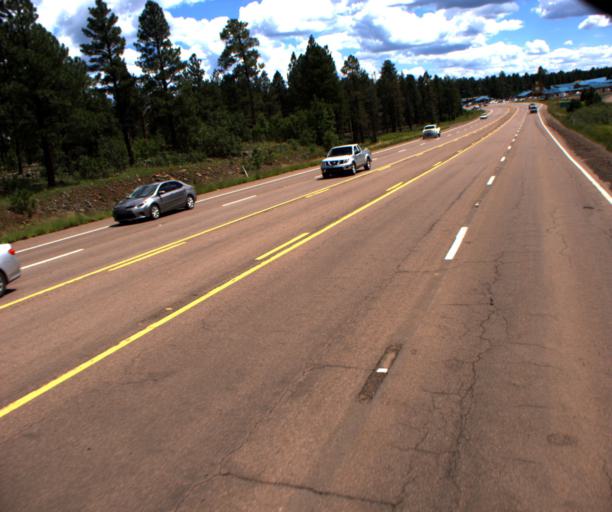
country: US
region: Arizona
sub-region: Navajo County
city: Pinetop-Lakeside
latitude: 34.0837
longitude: -109.9067
